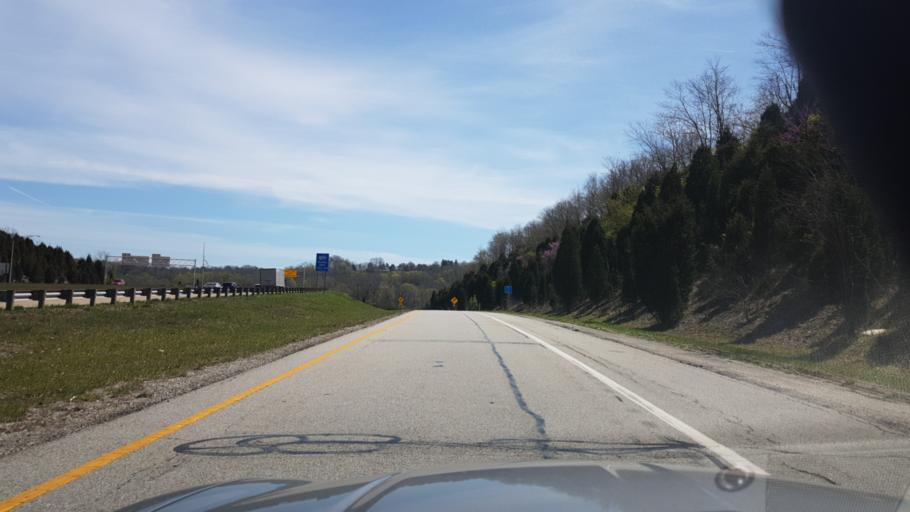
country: US
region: Kentucky
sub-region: Campbell County
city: Silver Grove
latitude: 39.0544
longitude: -84.3962
